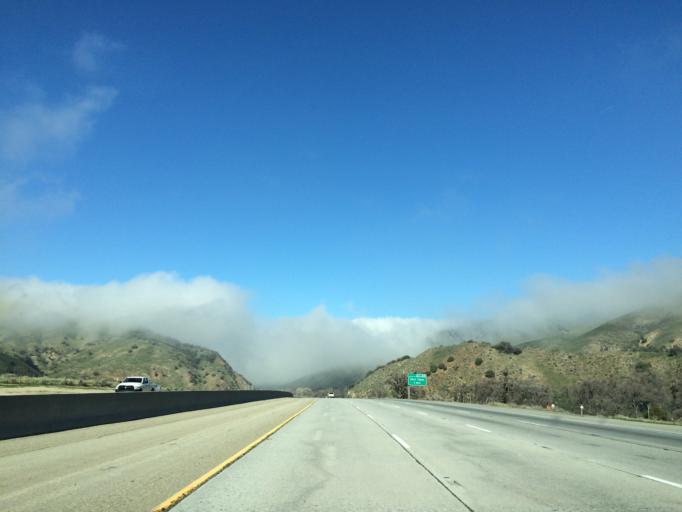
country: US
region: California
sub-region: Kern County
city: Lebec
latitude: 34.8612
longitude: -118.8787
